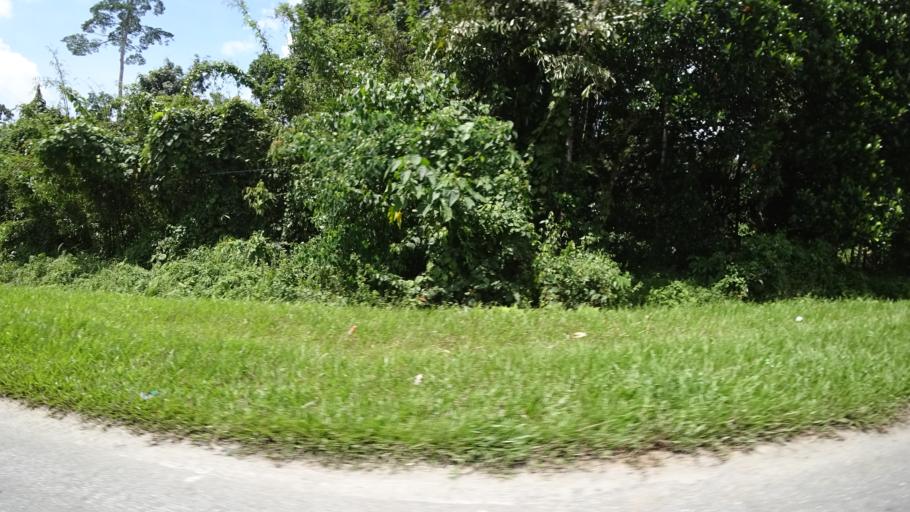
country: BN
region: Tutong
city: Tutong
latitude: 4.6818
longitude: 114.8102
